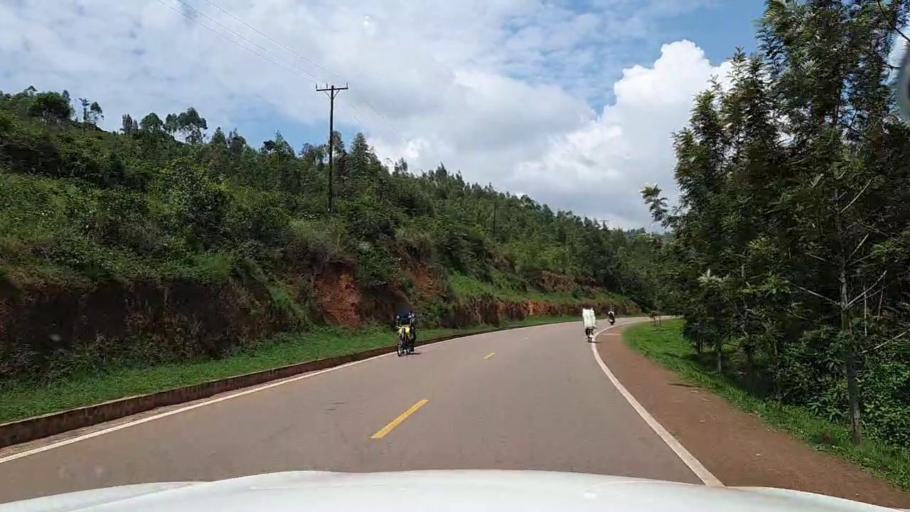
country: RW
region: Kigali
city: Kigali
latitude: -1.8423
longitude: 30.0862
